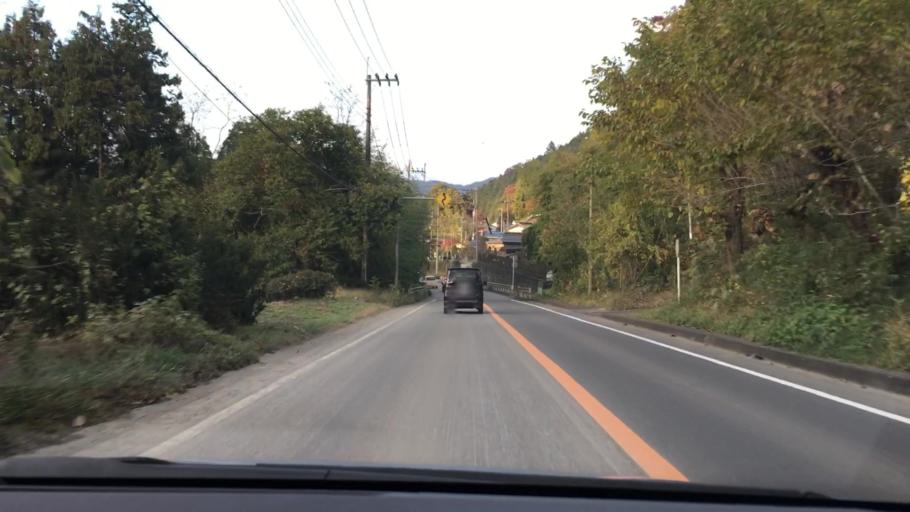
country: JP
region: Yamanashi
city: Uenohara
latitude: 35.5680
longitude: 139.2199
